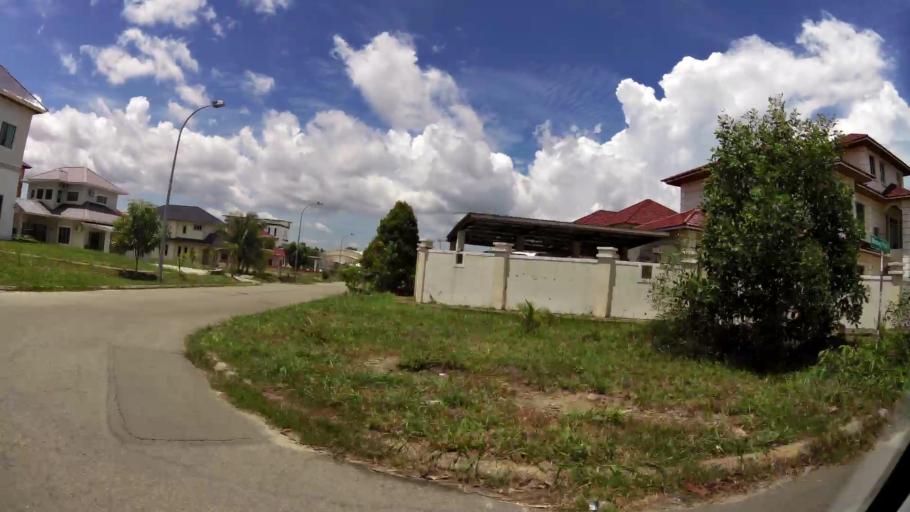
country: BN
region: Brunei and Muara
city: Bandar Seri Begawan
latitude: 4.9676
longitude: 114.9013
